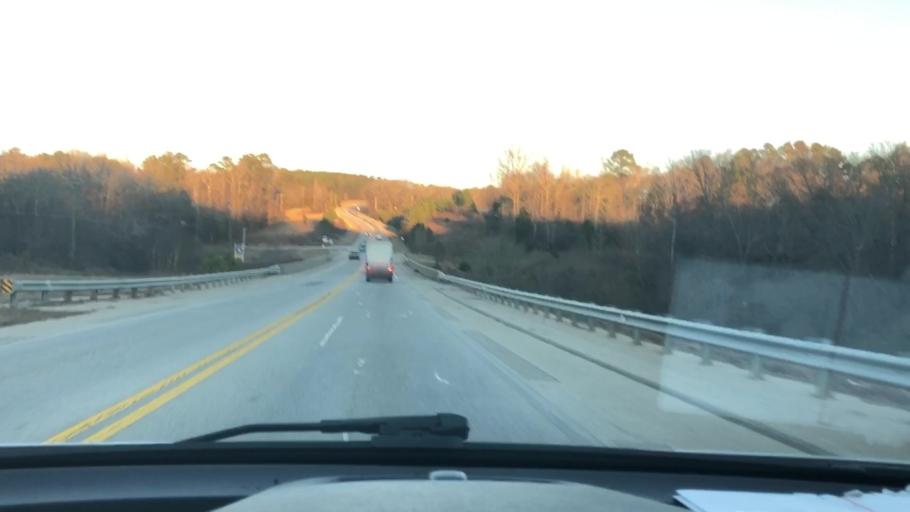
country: US
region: Georgia
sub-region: Walton County
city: Loganville
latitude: 33.8812
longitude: -83.8253
